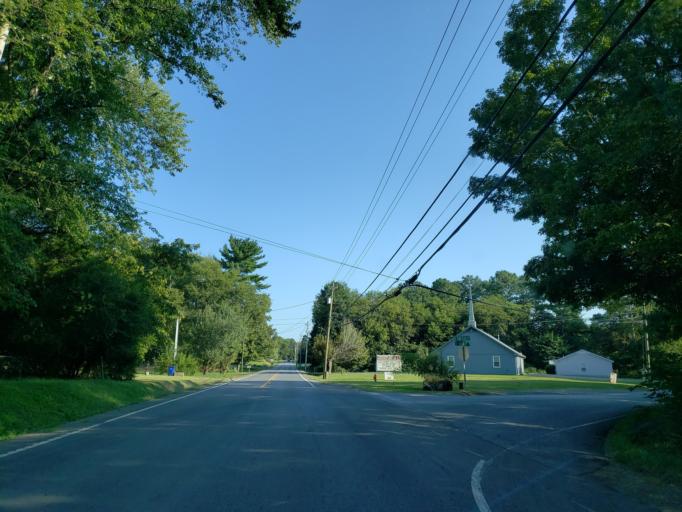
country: US
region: Tennessee
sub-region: Bradley County
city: Wildwood Lake
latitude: 35.0735
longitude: -84.8145
